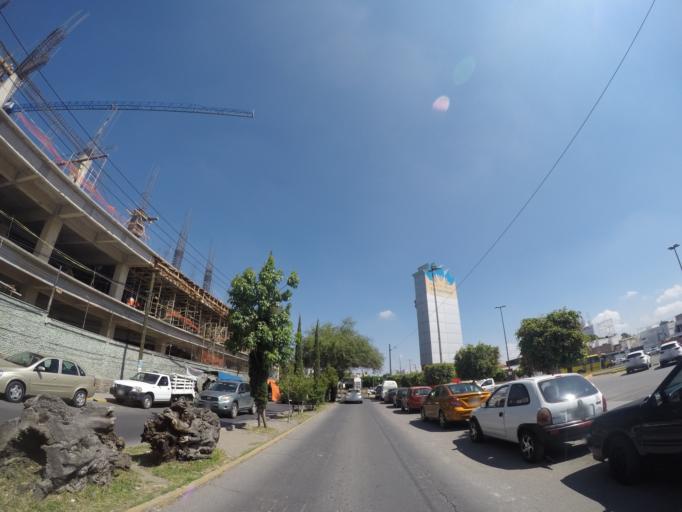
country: MX
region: San Luis Potosi
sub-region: San Luis Potosi
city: San Luis Potosi
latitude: 22.1475
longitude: -101.0142
